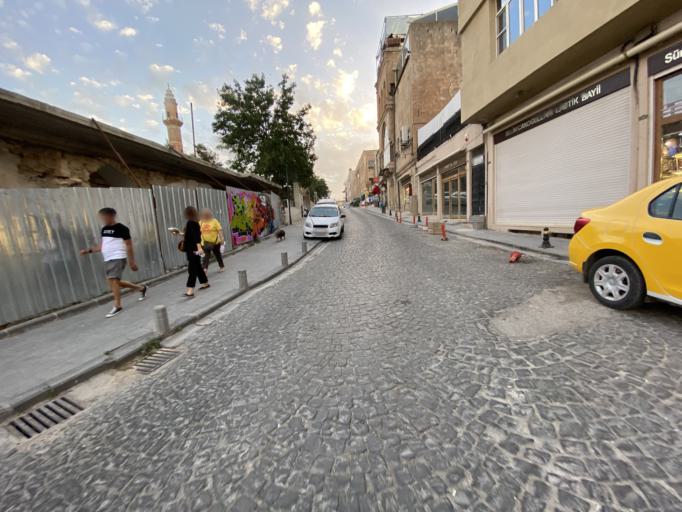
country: TR
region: Mardin
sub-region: Mardin Ilcesi
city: Mardin
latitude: 37.3144
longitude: 40.7439
